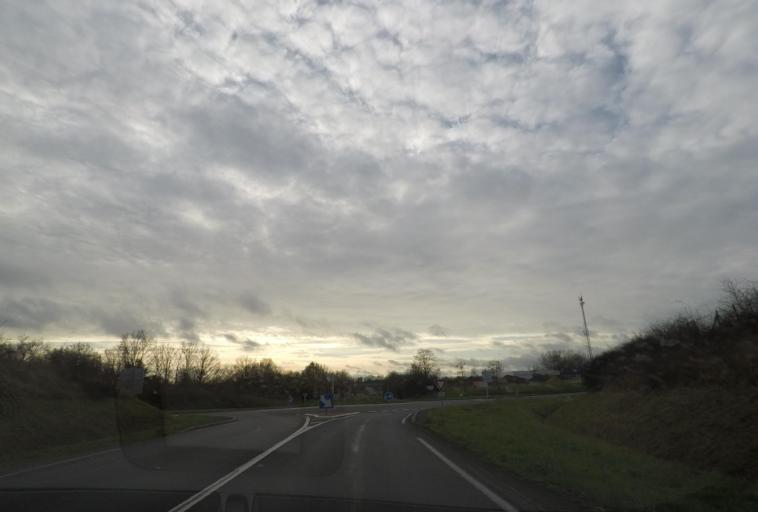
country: FR
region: Pays de la Loire
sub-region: Departement de la Sarthe
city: Saint-Calais
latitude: 47.9269
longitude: 0.7608
